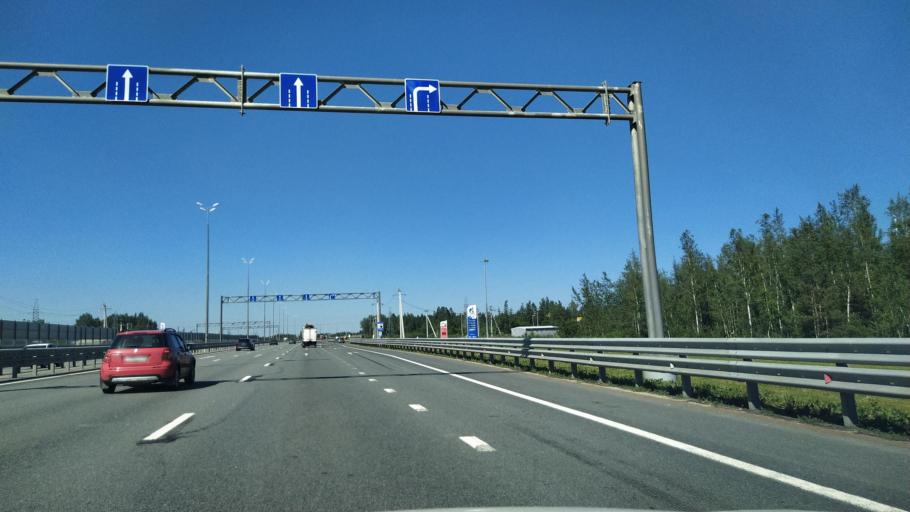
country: RU
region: Leningrad
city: Gatchina
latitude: 59.5713
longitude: 30.1700
